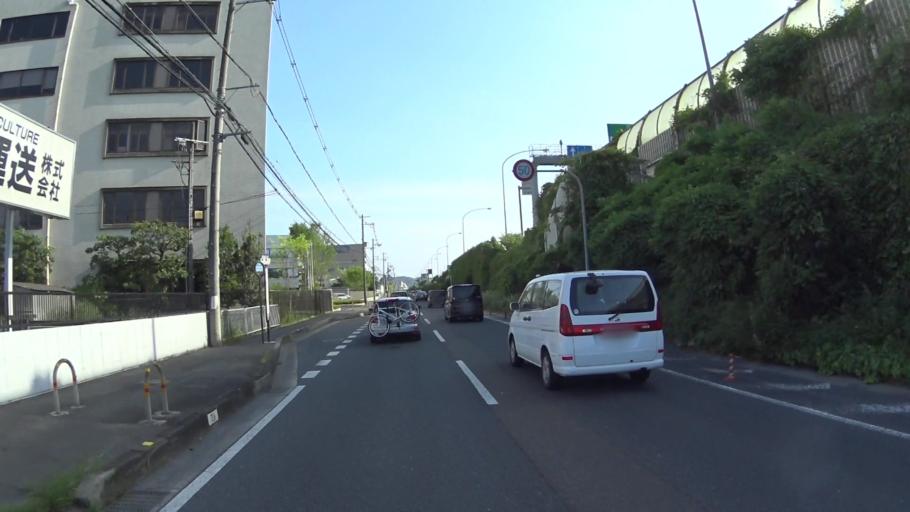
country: JP
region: Kyoto
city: Muko
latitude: 34.9215
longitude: 135.7147
